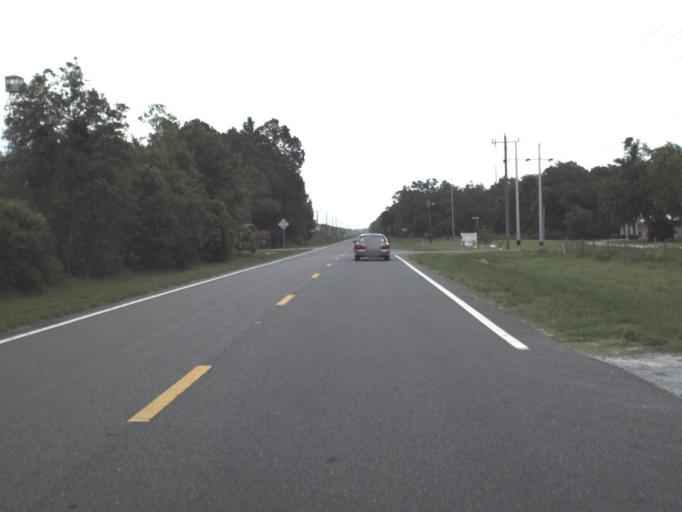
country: US
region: Florida
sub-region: Levy County
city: Chiefland
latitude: 29.2370
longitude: -82.9370
